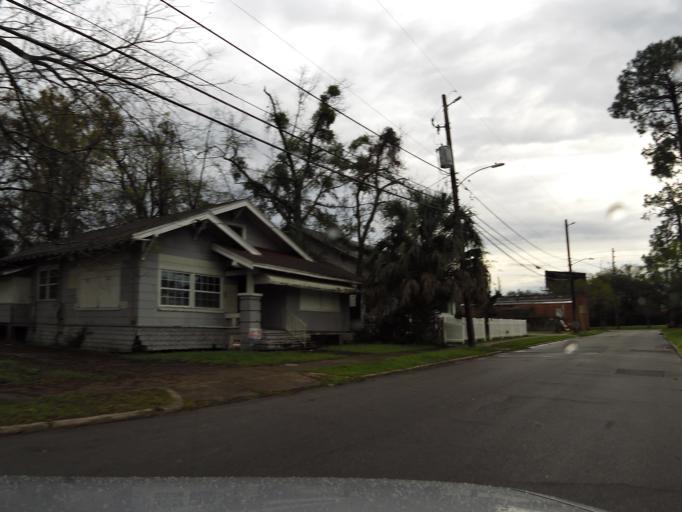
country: US
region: Florida
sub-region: Duval County
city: Jacksonville
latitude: 30.3233
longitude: -81.6975
